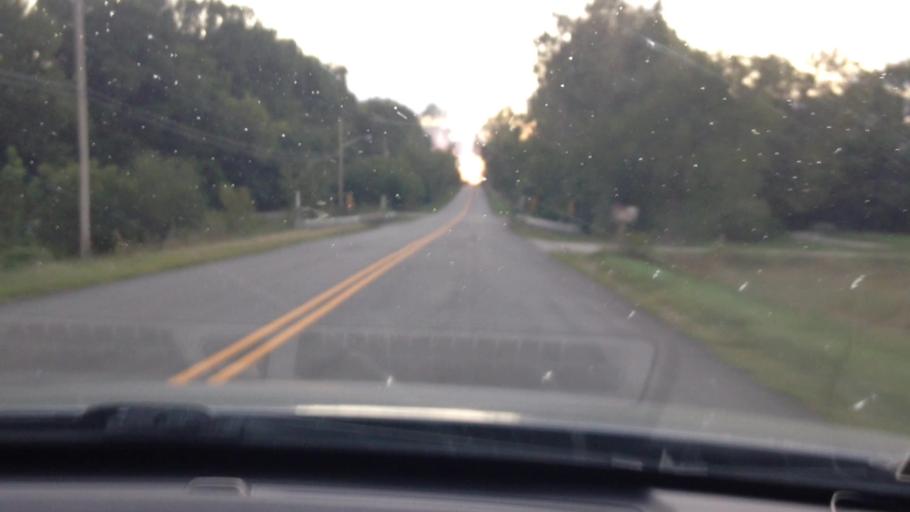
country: US
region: Kansas
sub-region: Leavenworth County
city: Lansing
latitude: 39.1867
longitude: -94.8701
